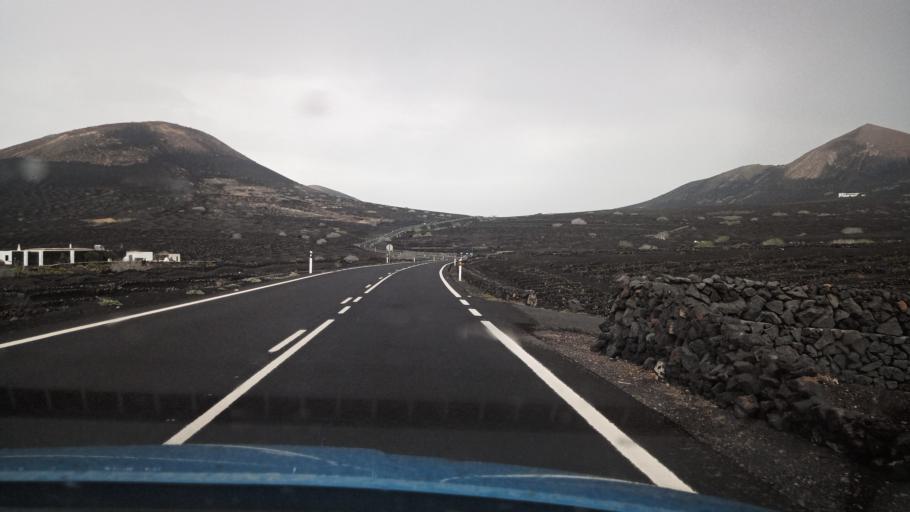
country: ES
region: Canary Islands
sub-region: Provincia de Las Palmas
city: Yaiza
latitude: 28.9597
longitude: -13.7301
